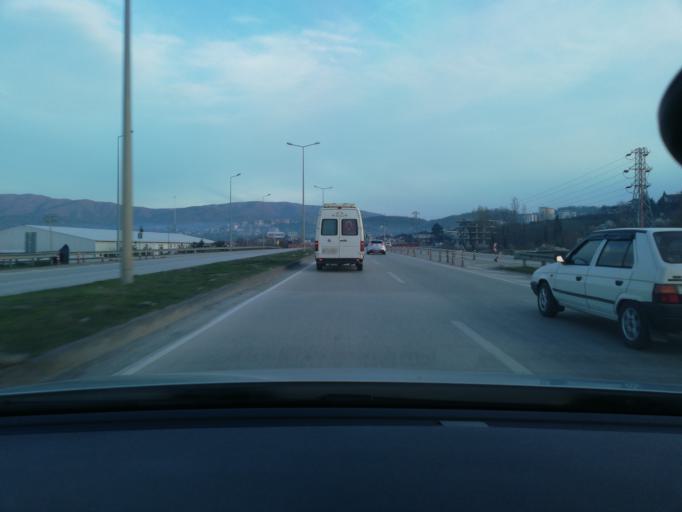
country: TR
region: Duzce
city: Konuralp
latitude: 40.8902
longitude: 31.1686
